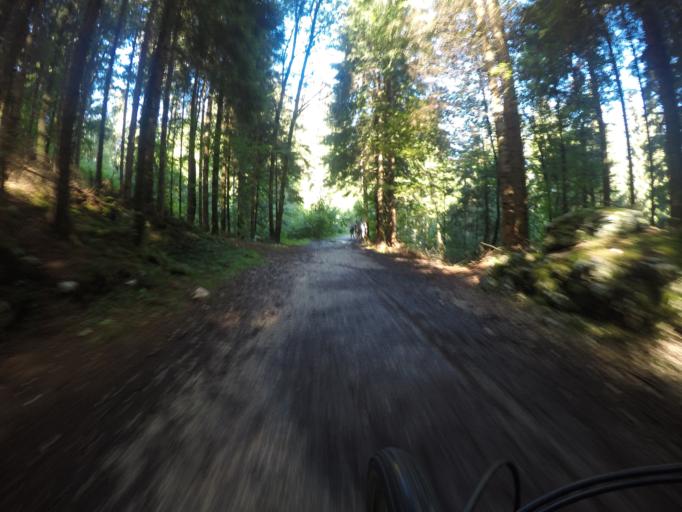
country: IT
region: Veneto
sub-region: Provincia di Vicenza
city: Canove di Roana
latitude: 45.8389
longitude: 11.4434
